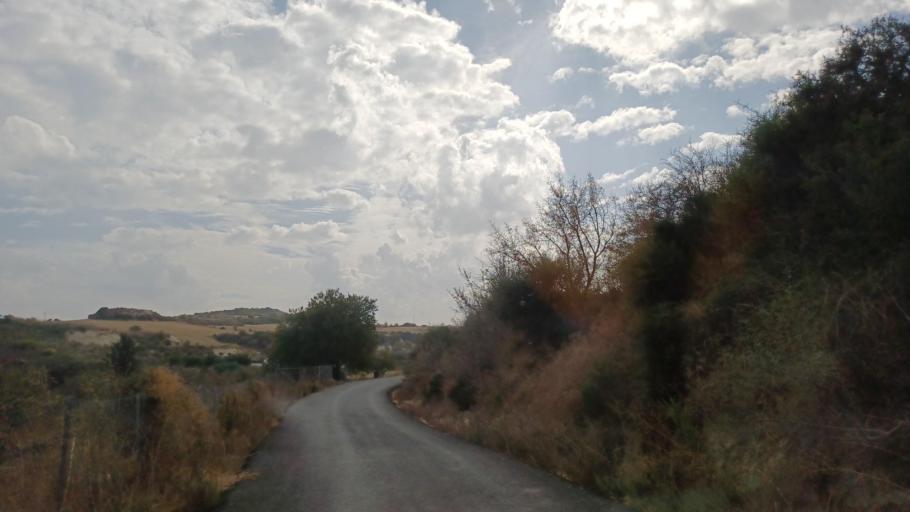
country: CY
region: Pafos
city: Polis
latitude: 35.0143
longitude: 32.4139
